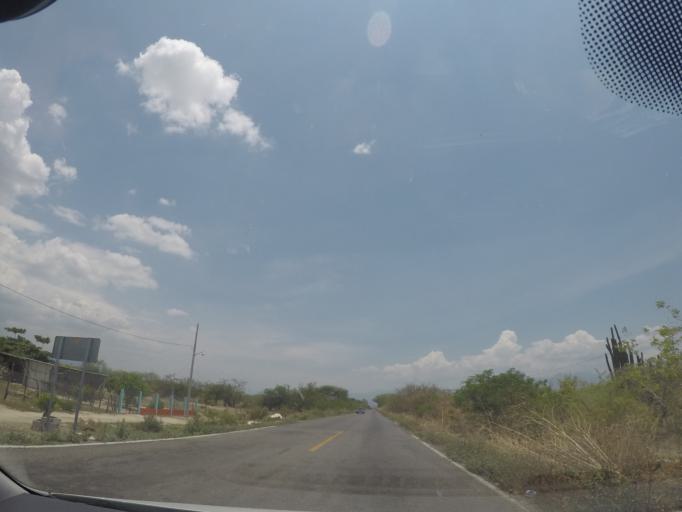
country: MX
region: Oaxaca
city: Santa Maria Jalapa del Marques
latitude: 16.4398
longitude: -95.4695
